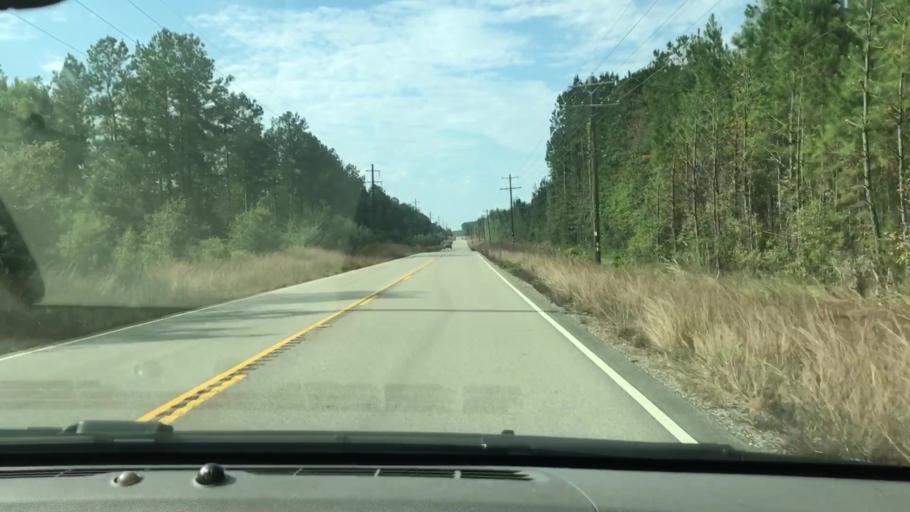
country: US
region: Louisiana
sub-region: Saint Tammany Parish
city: Abita Springs
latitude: 30.5325
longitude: -89.9076
